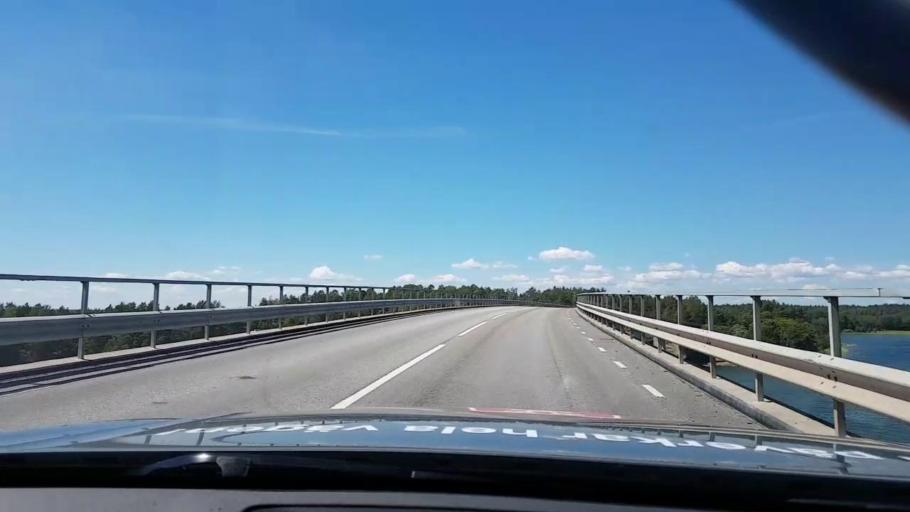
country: SE
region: Kalmar
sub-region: Vasterviks Kommun
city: Forserum
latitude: 57.9189
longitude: 16.5927
